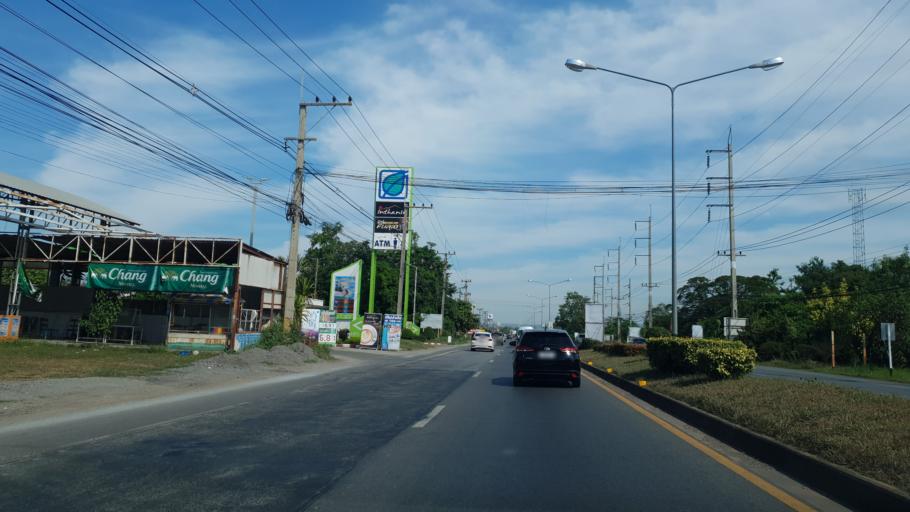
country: TH
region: Phitsanulok
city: Wang Thong
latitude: 16.8509
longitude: 100.3472
